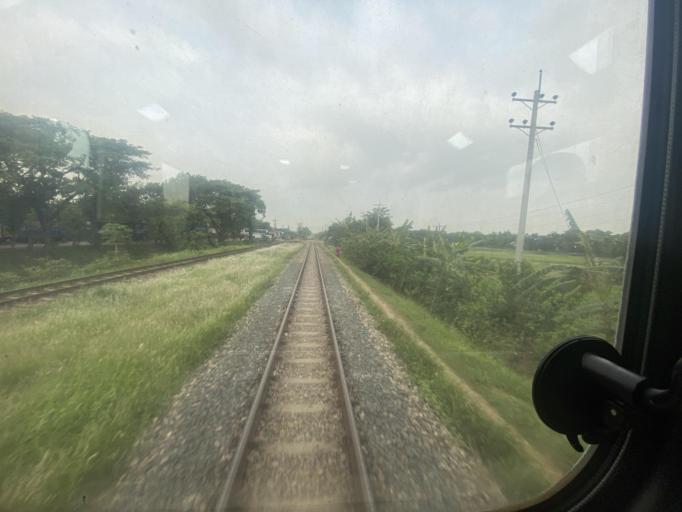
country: BD
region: Dhaka
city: Tungi
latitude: 23.9324
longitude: 90.5214
